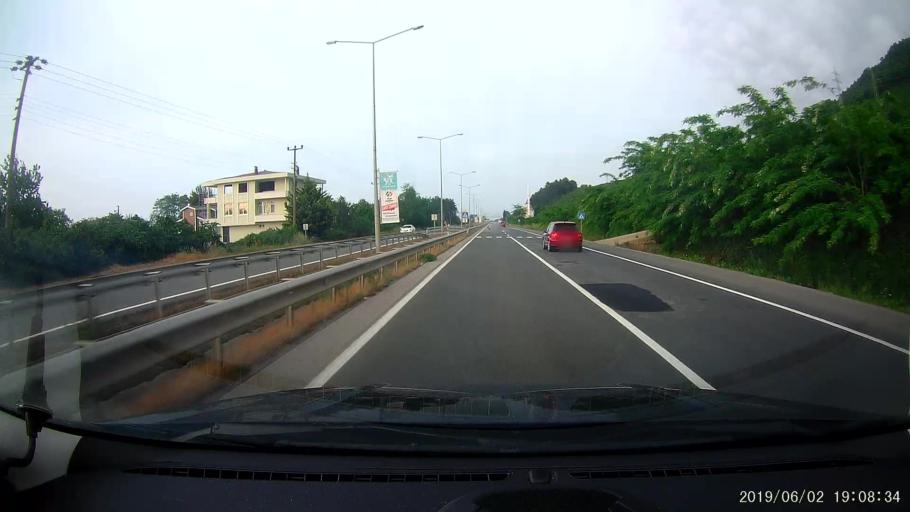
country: TR
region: Ordu
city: Gulyali
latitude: 40.9762
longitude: 38.0111
